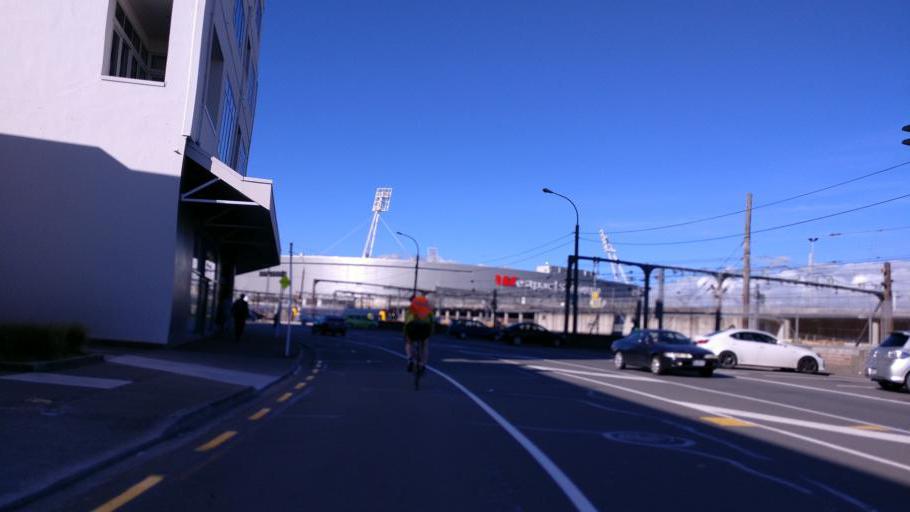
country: NZ
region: Wellington
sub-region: Wellington City
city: Wellington
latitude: -41.2755
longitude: 174.7830
